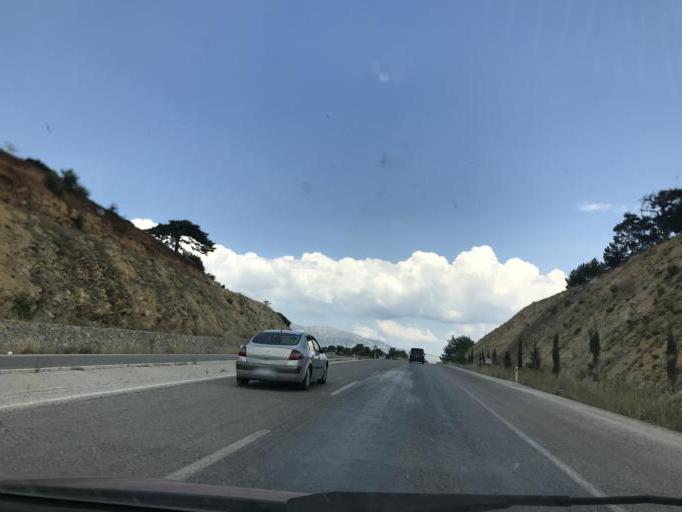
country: TR
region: Denizli
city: Tavas
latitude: 37.6150
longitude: 29.1640
